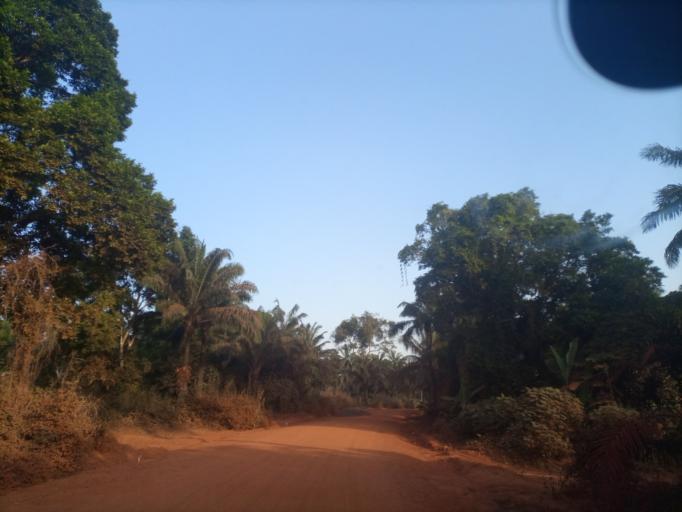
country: NG
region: Enugu
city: Obolo-Eke (1)
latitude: 6.7897
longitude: 7.5896
